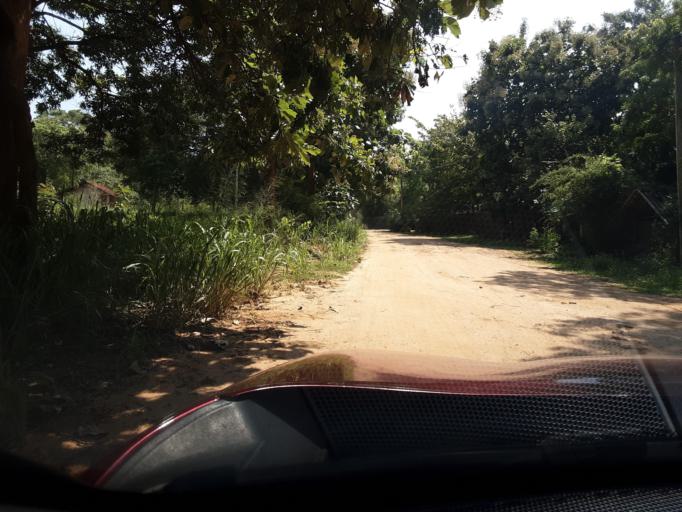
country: LK
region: Central
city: Sigiriya
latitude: 8.0021
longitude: 80.7474
